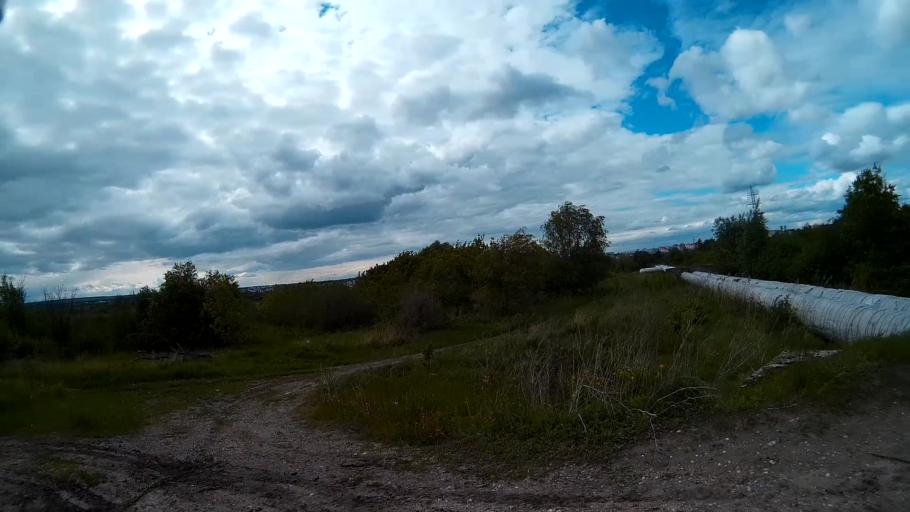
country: RU
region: Ulyanovsk
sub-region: Ulyanovskiy Rayon
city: Ulyanovsk
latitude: 54.2486
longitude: 48.3025
